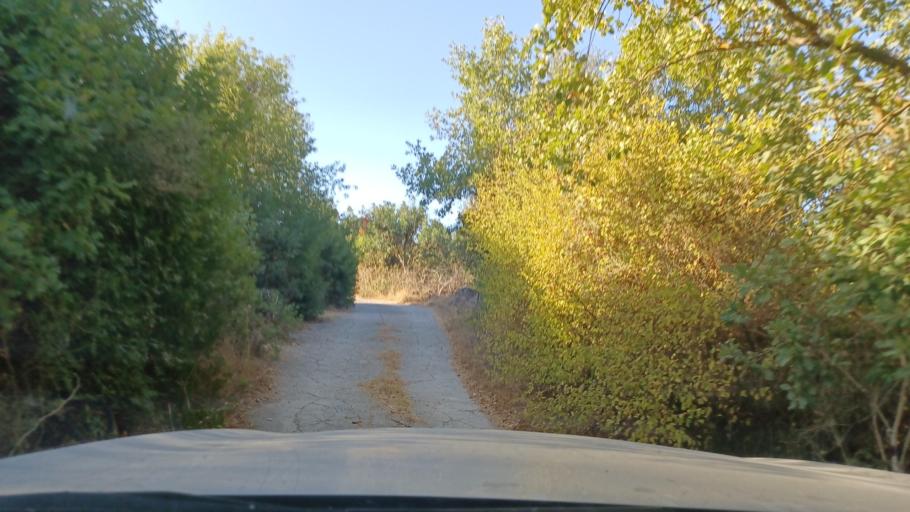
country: CY
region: Pafos
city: Polis
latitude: 34.9968
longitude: 32.4878
